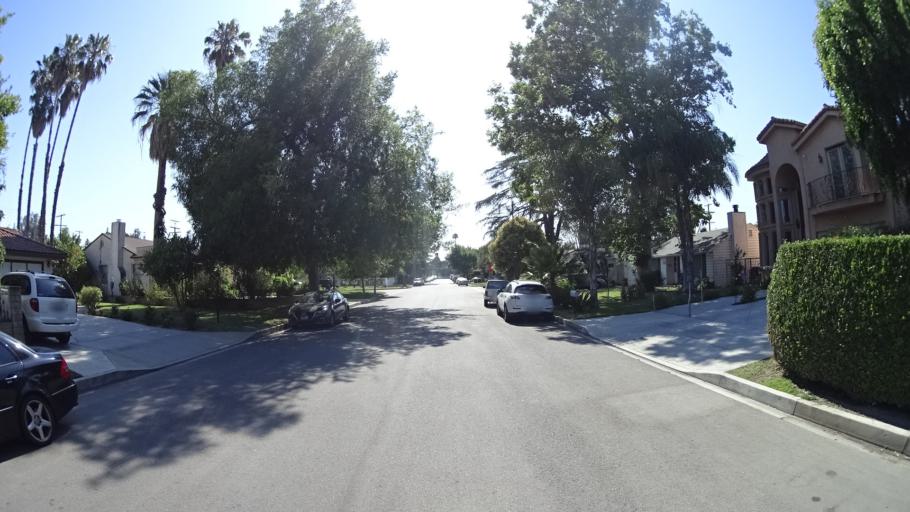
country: US
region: California
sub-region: Los Angeles County
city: Sherman Oaks
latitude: 34.1603
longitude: -118.4546
